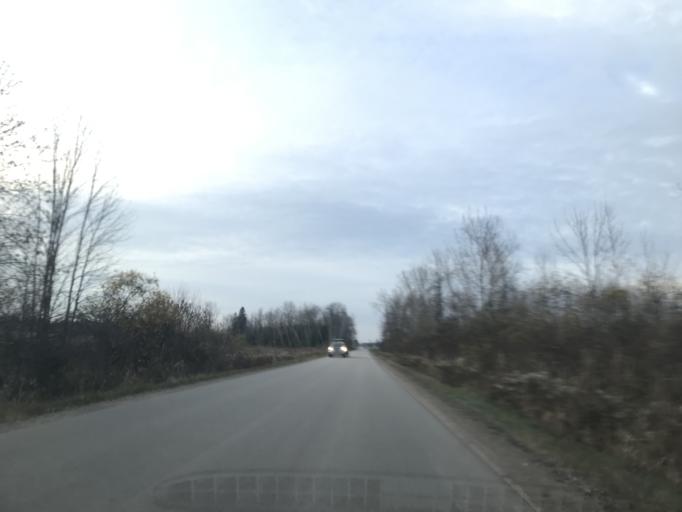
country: US
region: Wisconsin
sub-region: Marinette County
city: Peshtigo
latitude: 45.0892
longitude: -87.7995
